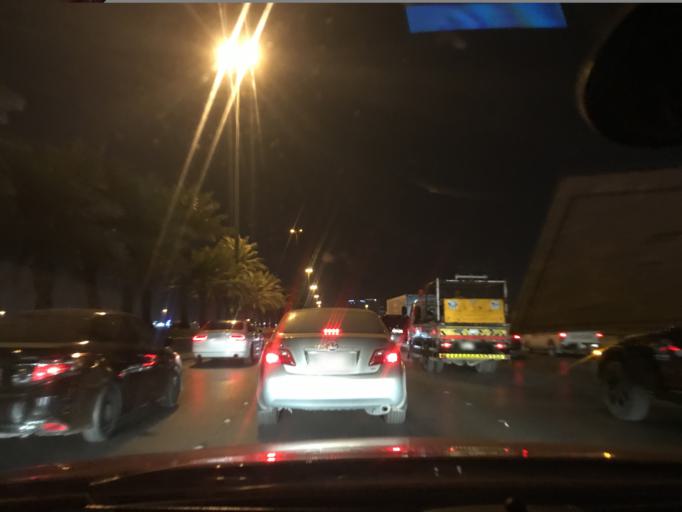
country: SA
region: Ar Riyad
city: Riyadh
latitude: 24.7698
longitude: 46.7339
